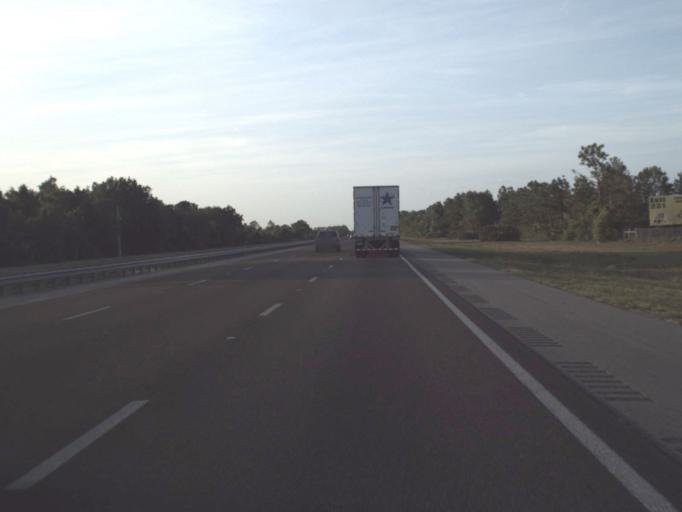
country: US
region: Florida
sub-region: Brevard County
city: Mims
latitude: 28.7435
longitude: -80.8859
